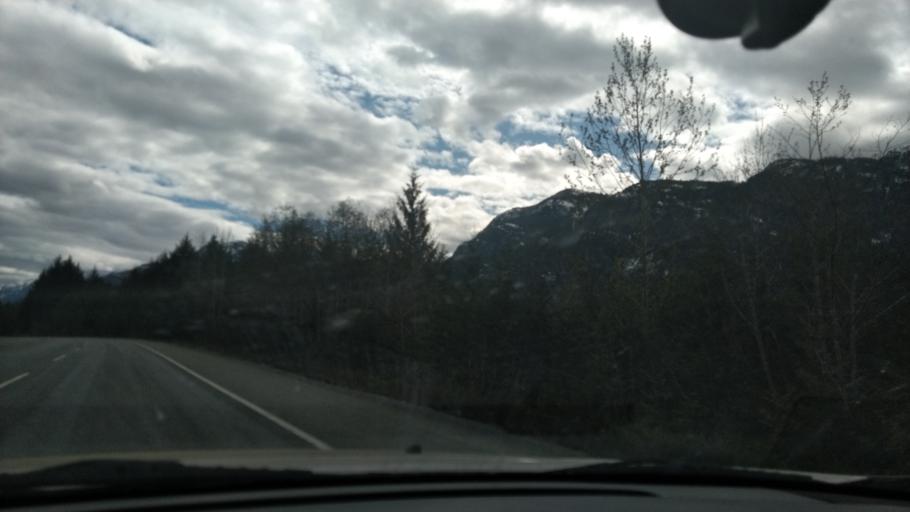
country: CA
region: British Columbia
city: Campbell River
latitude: 49.8604
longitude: -125.6247
